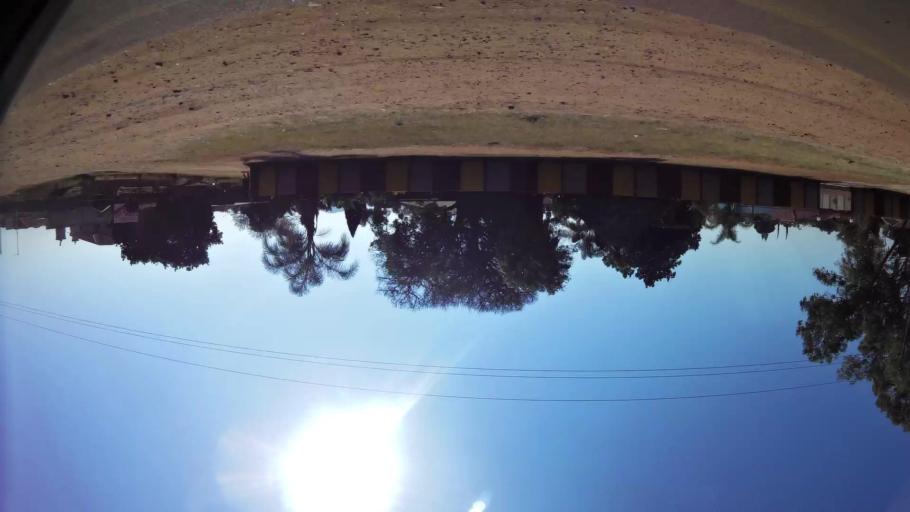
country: ZA
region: North-West
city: Ga-Rankuwa
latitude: -25.6701
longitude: 28.0930
